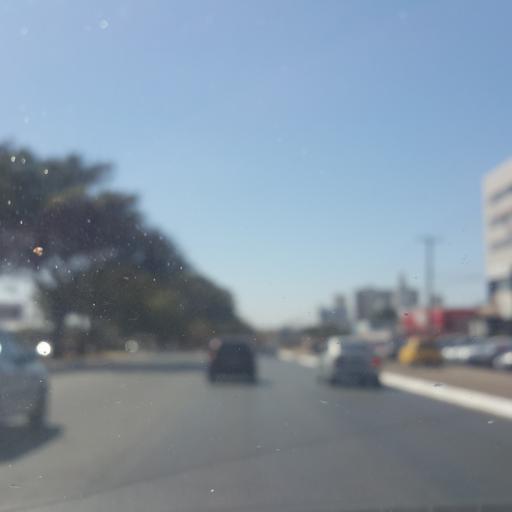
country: BR
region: Federal District
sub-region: Brasilia
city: Brasilia
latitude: -15.8101
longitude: -48.0894
